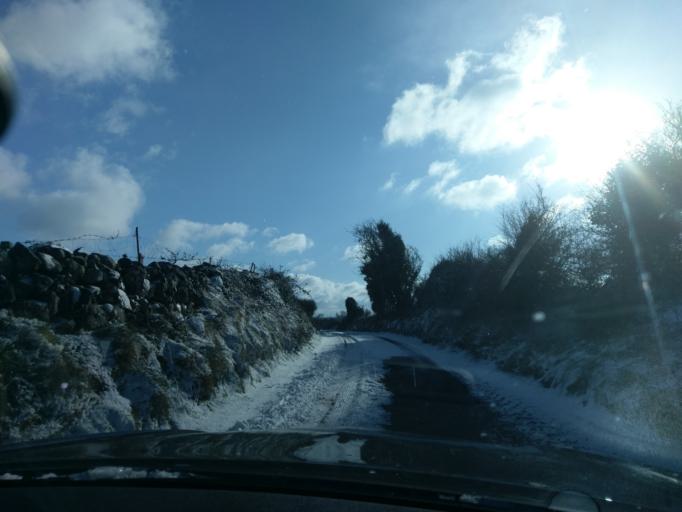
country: IE
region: Connaught
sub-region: County Galway
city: Athenry
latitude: 53.1971
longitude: -8.7499
